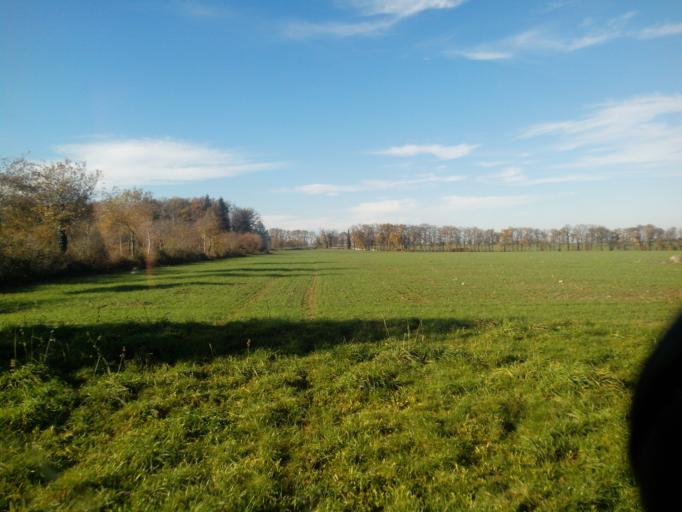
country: FR
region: Limousin
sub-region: Departement de la Haute-Vienne
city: Nantiat
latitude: 46.0500
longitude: 1.1117
